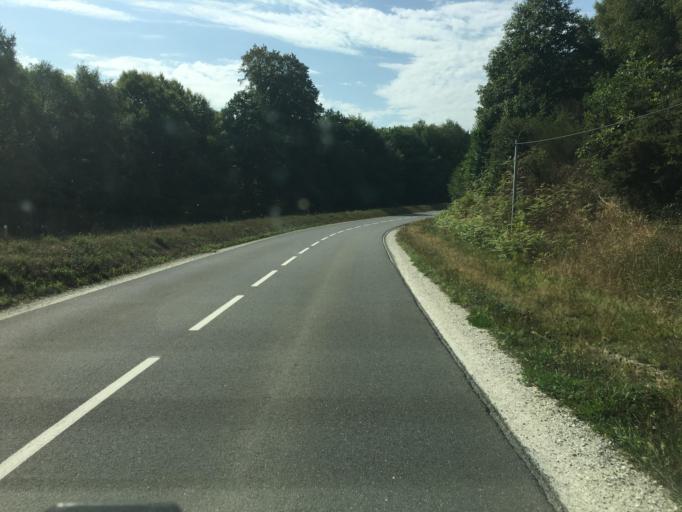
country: FR
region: Brittany
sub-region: Departement des Cotes-d'Armor
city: Gouarec
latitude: 48.2200
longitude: -3.1669
